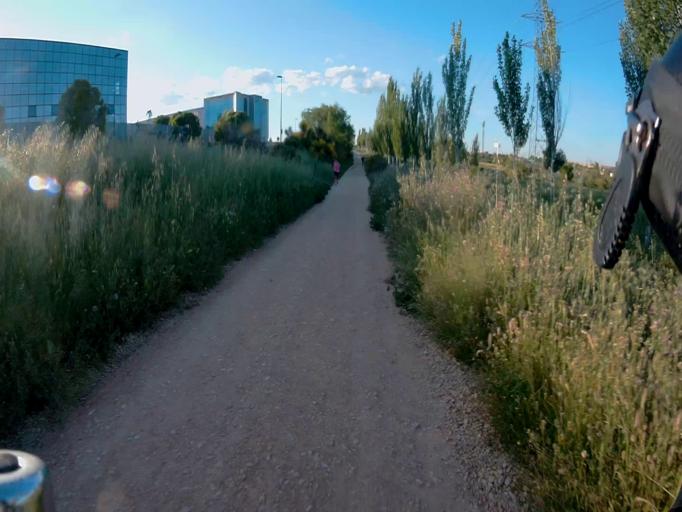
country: ES
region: Madrid
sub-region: Provincia de Madrid
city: Fuenlabrada
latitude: 40.3083
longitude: -3.7983
